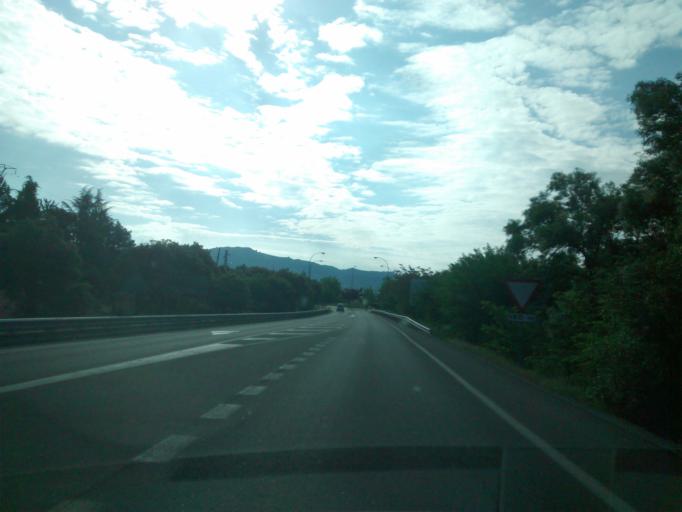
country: ES
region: Madrid
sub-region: Provincia de Madrid
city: Alpedrete
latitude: 40.6517
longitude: -4.0110
